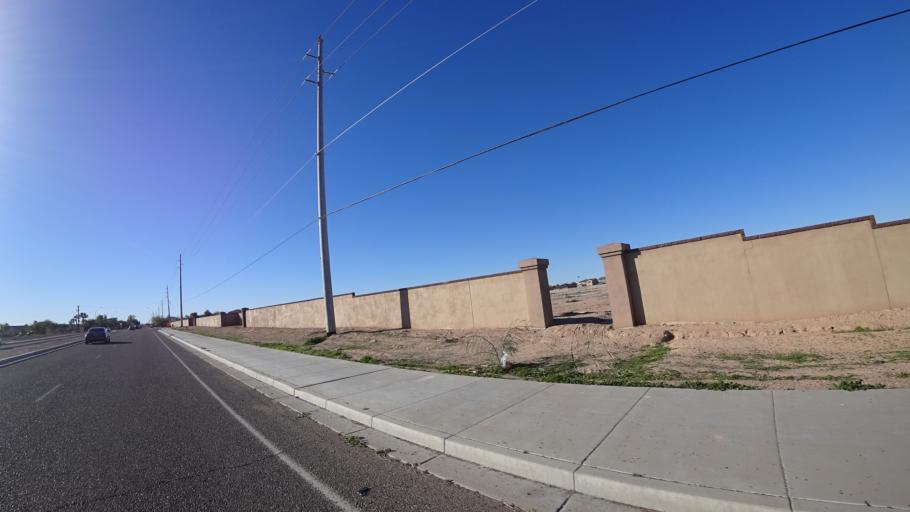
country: US
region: Arizona
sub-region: Maricopa County
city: Goodyear
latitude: 33.4500
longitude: -112.3961
